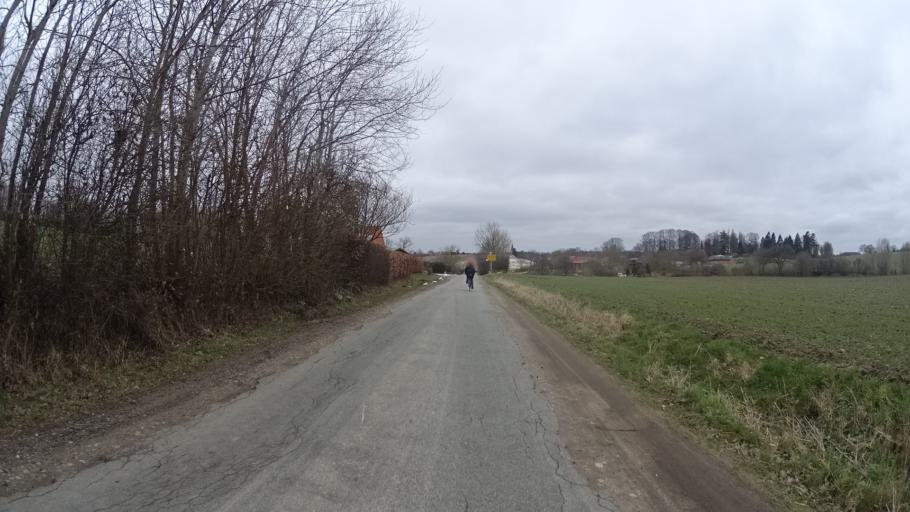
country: DE
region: Schleswig-Holstein
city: Neukirchen
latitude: 54.2227
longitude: 10.5618
